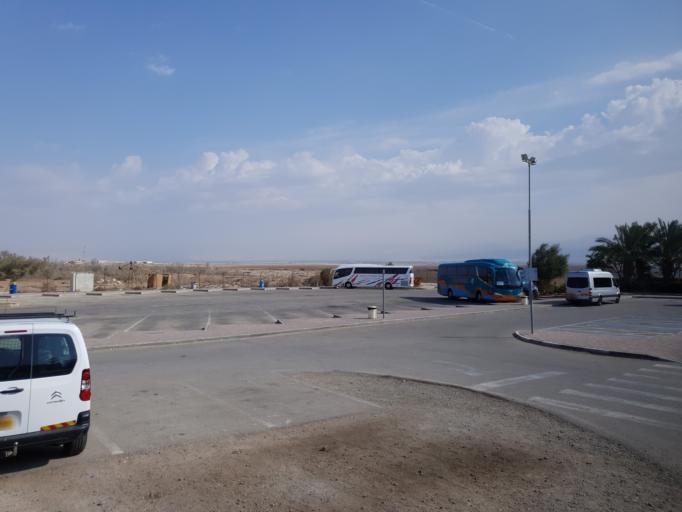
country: PS
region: West Bank
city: Jericho
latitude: 31.7639
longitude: 35.5029
